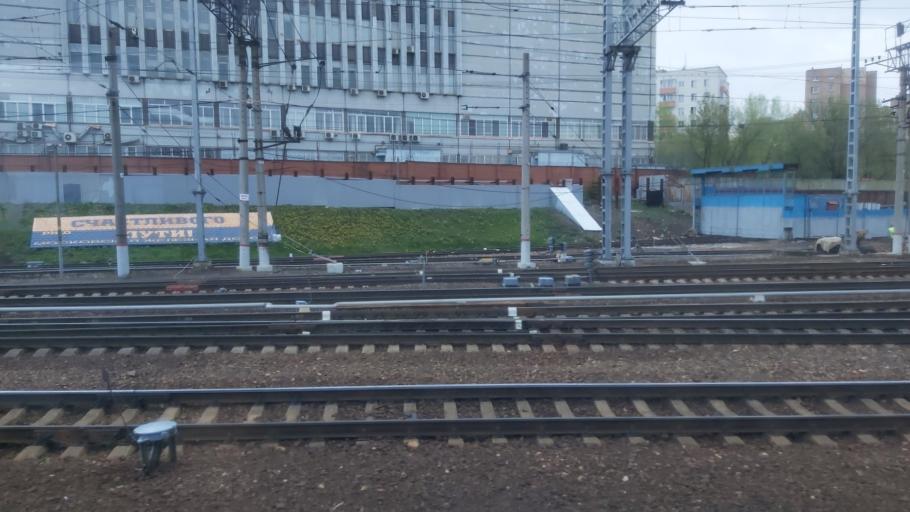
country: RU
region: Moscow
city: Sokol'niki
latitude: 55.7865
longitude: 37.6527
